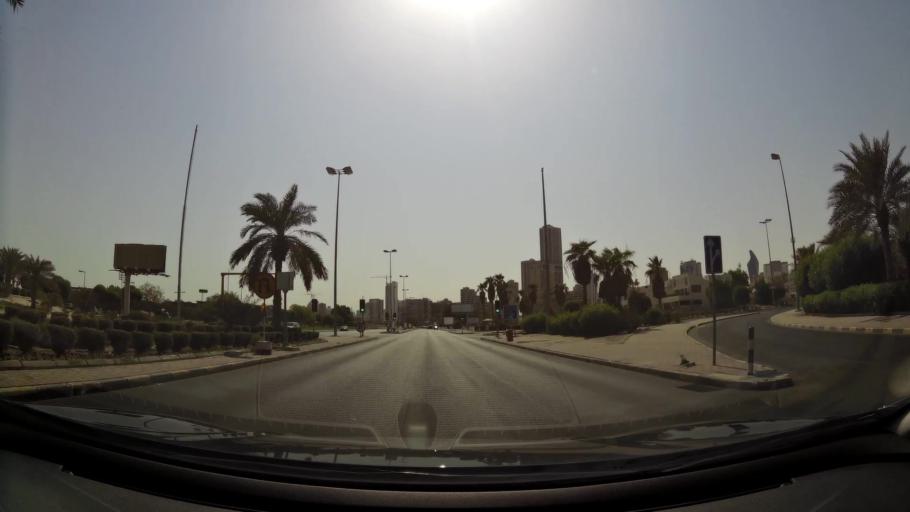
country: KW
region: Al Asimah
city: Ad Dasmah
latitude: 29.3827
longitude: 48.0027
